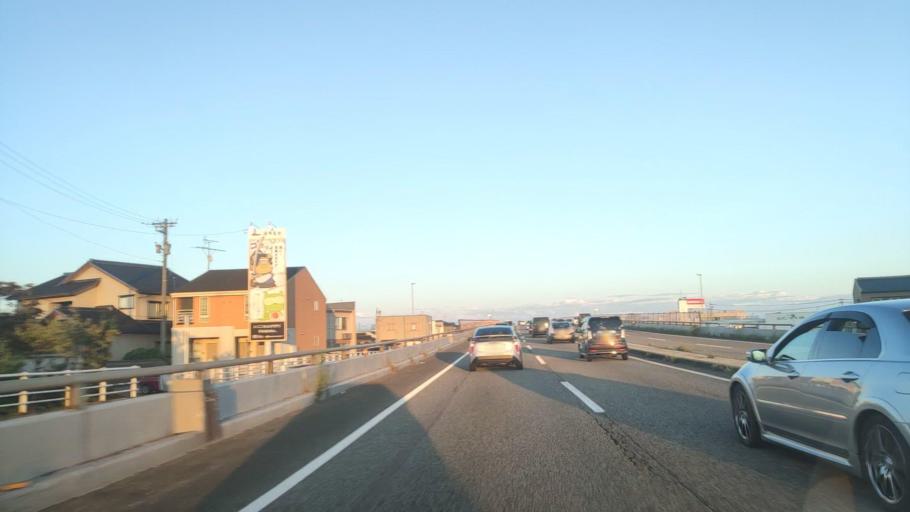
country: JP
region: Toyama
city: Takaoka
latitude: 36.7605
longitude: 137.0244
